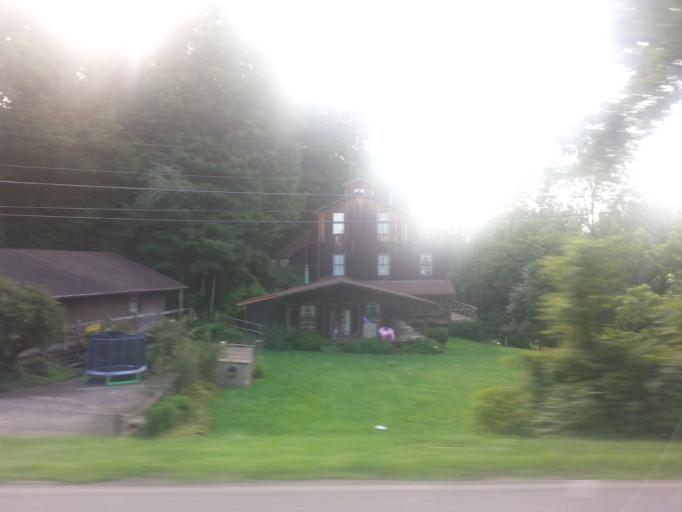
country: US
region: Tennessee
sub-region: Blount County
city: Wildwood
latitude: 35.7991
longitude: -83.8899
